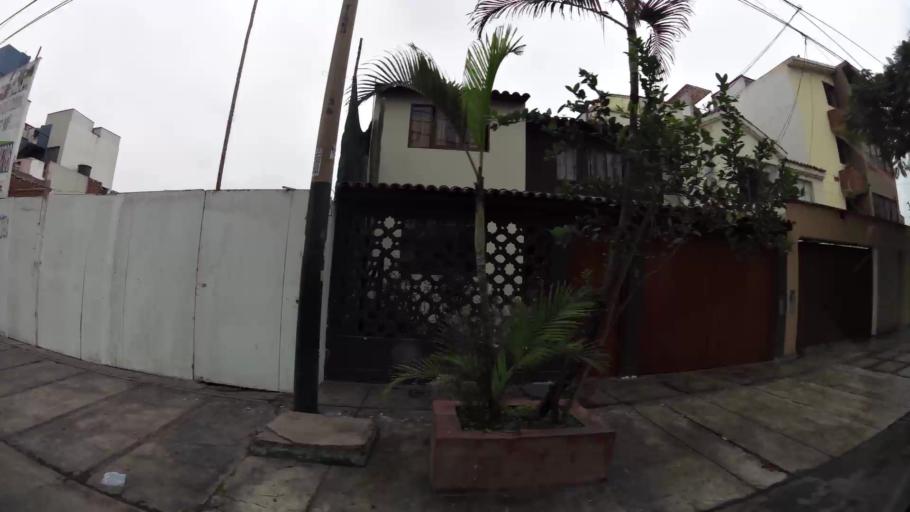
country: PE
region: Lima
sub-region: Lima
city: Surco
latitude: -12.1363
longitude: -77.0034
